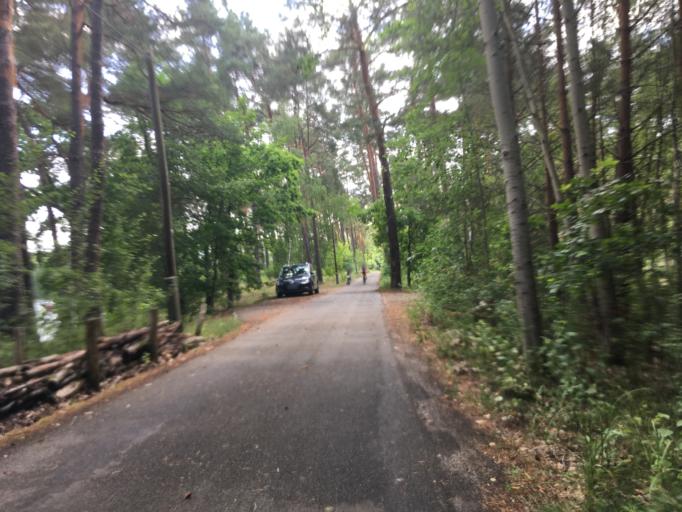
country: DE
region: Berlin
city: Muggelheim
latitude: 52.3964
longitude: 13.6525
